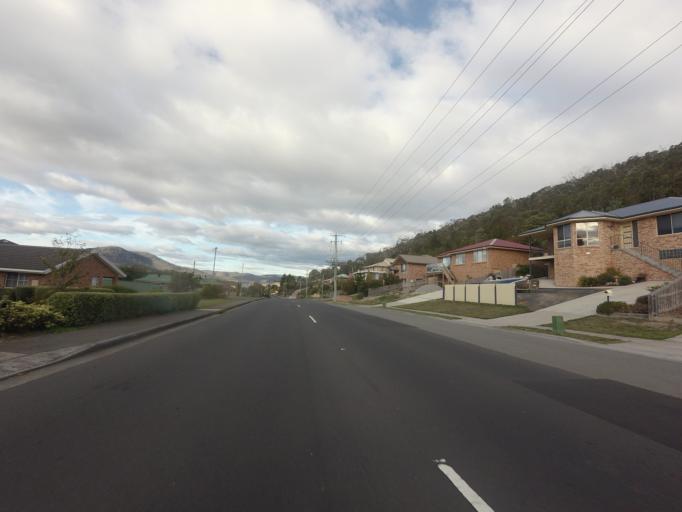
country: AU
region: Tasmania
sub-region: Glenorchy
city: Berriedale
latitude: -42.8239
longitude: 147.2523
